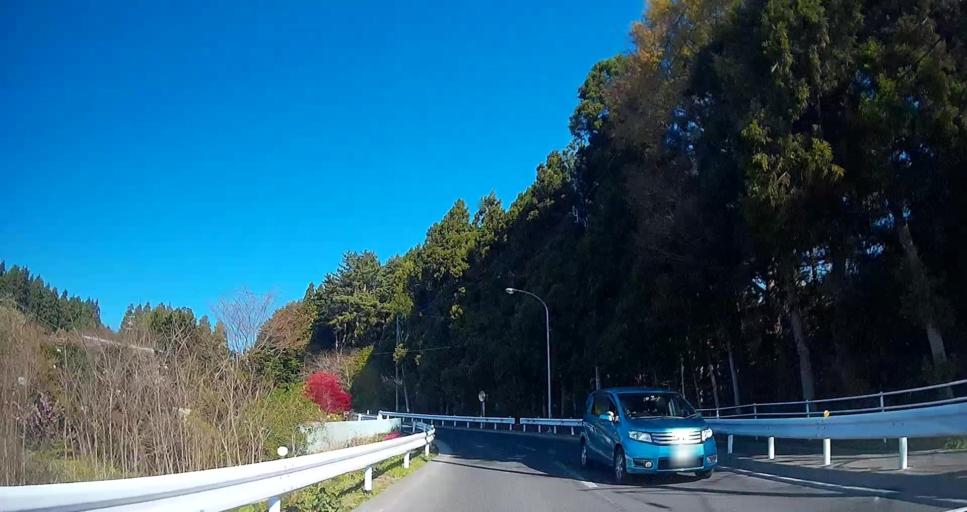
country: JP
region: Aomori
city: Hachinohe
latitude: 40.5193
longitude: 141.5824
